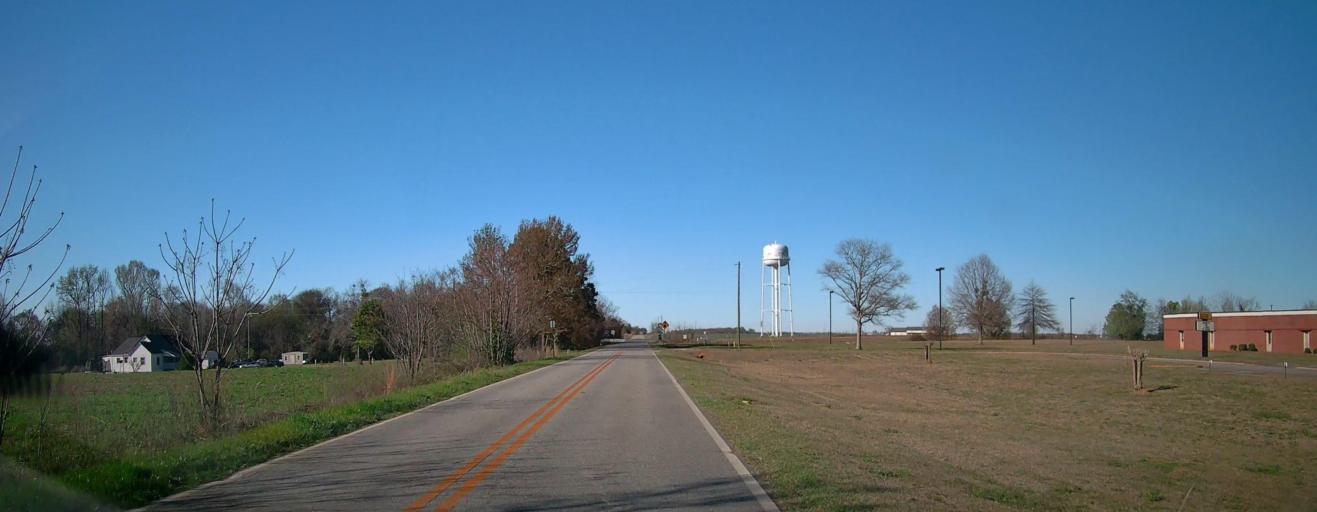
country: US
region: Georgia
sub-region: Peach County
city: Fort Valley
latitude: 32.5690
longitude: -83.9157
